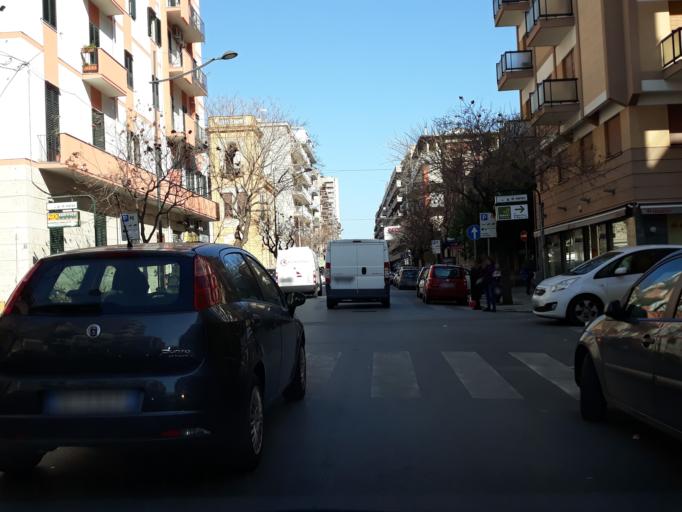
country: IT
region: Sicily
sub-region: Palermo
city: Palermo
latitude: 38.1335
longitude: 13.3463
